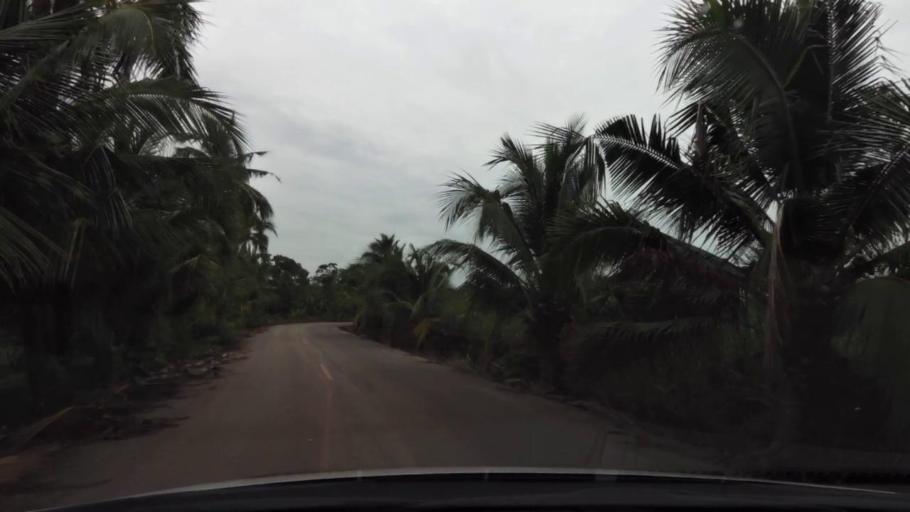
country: TH
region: Samut Sakhon
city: Ban Phaeo
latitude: 13.5881
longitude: 100.0350
